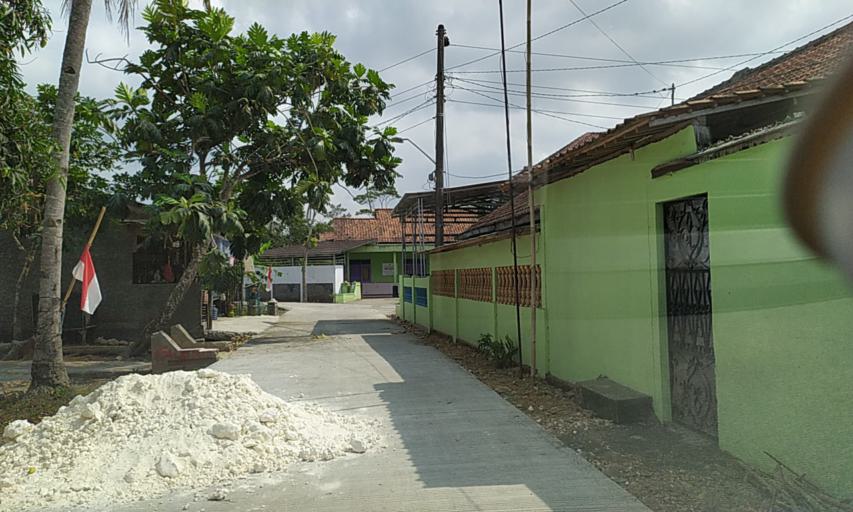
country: ID
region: Central Java
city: Kauman
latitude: -7.4799
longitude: 108.7854
